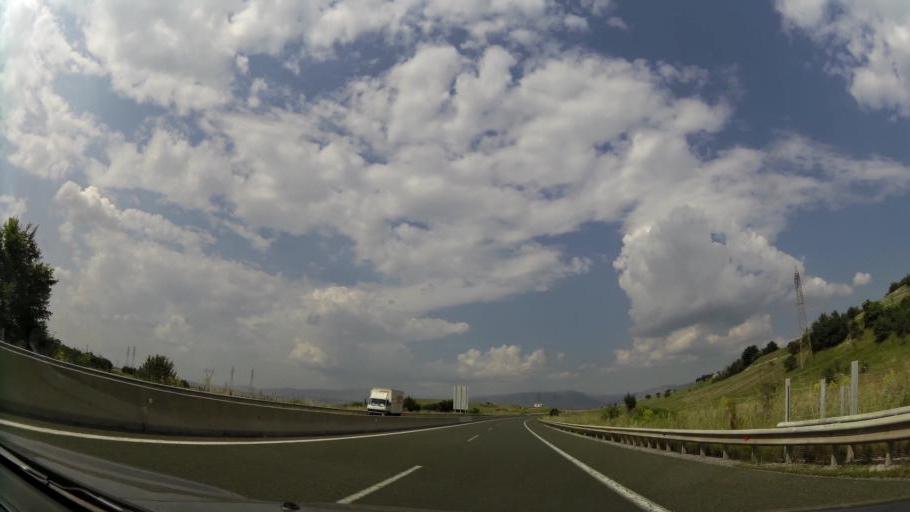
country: GR
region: West Macedonia
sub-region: Nomos Kozanis
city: Koila
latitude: 40.3578
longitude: 21.8148
